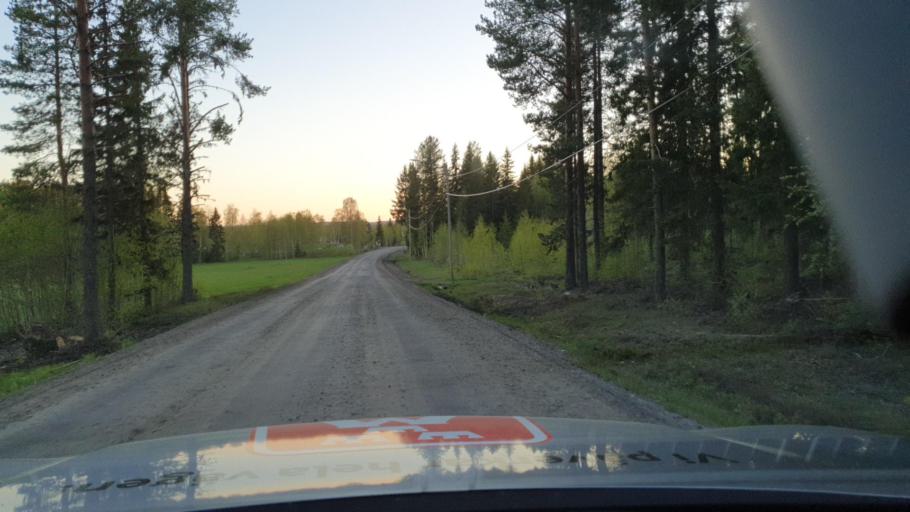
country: SE
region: Vaesternorrland
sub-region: OErnskoeldsviks Kommun
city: Ornskoldsvik
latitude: 63.5267
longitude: 18.5470
